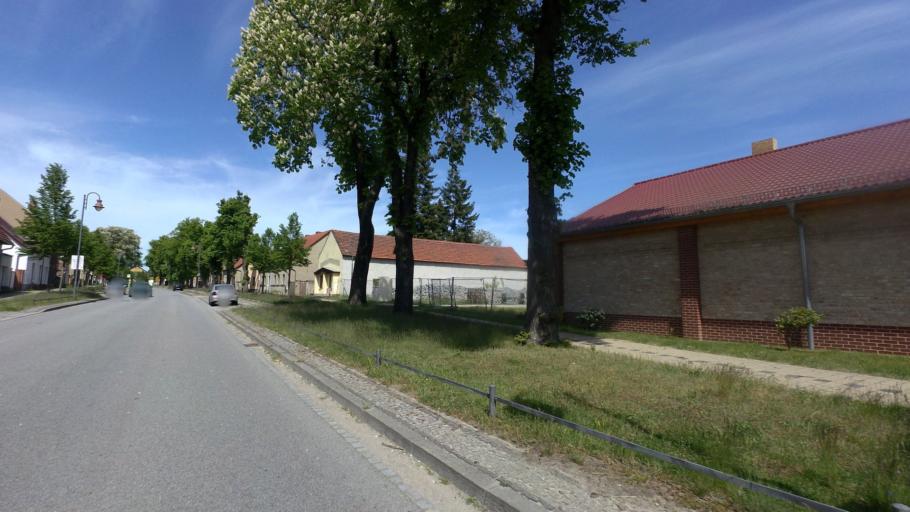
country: DE
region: Brandenburg
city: Sperenberg
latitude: 52.1380
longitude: 13.3657
